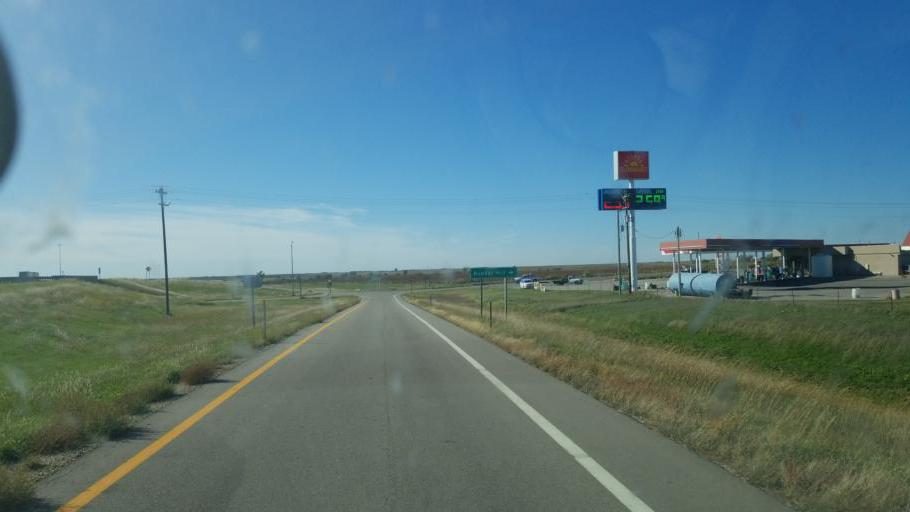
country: US
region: Kansas
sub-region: Russell County
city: Russell
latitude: 38.8576
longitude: -98.7050
